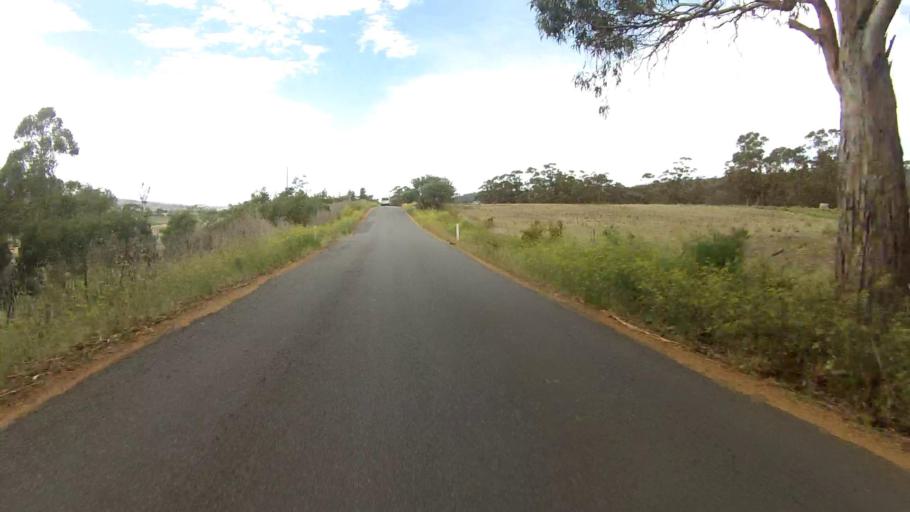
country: AU
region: Tasmania
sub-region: Clarence
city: Lindisfarne
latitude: -42.7507
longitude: 147.3751
